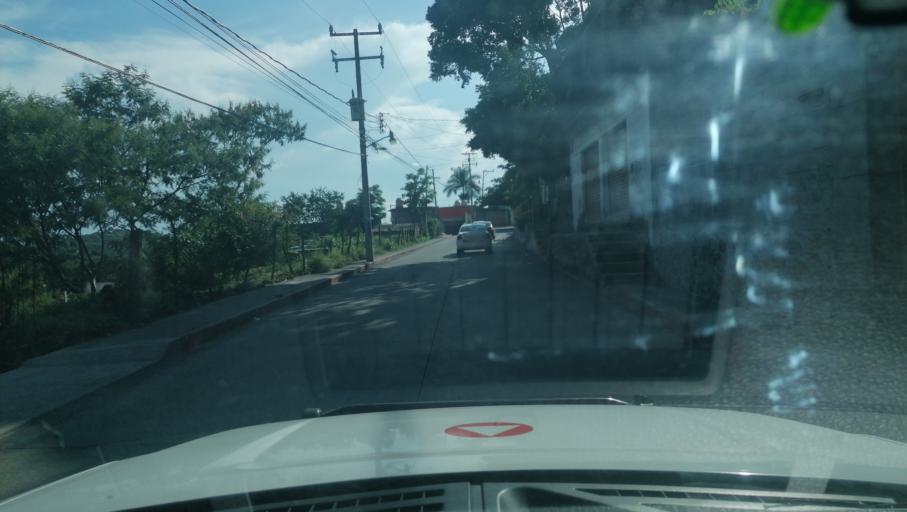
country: MX
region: Morelos
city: Emiliano Zapata
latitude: 18.8360
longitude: -99.1897
